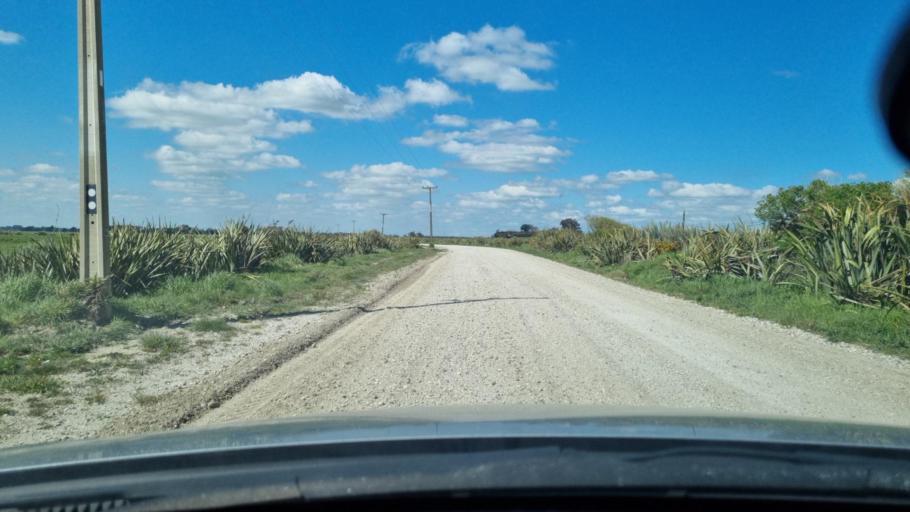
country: NZ
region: Southland
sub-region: Invercargill City
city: Invercargill
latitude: -46.3932
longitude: 168.2451
